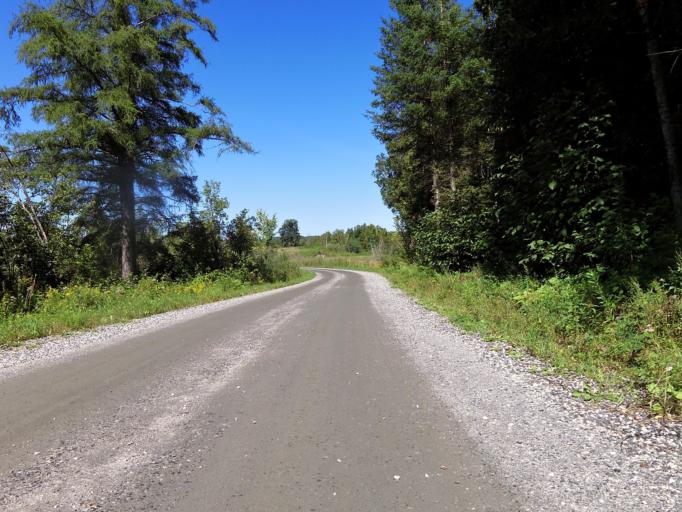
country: CA
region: Ontario
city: Renfrew
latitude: 45.1287
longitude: -76.6848
